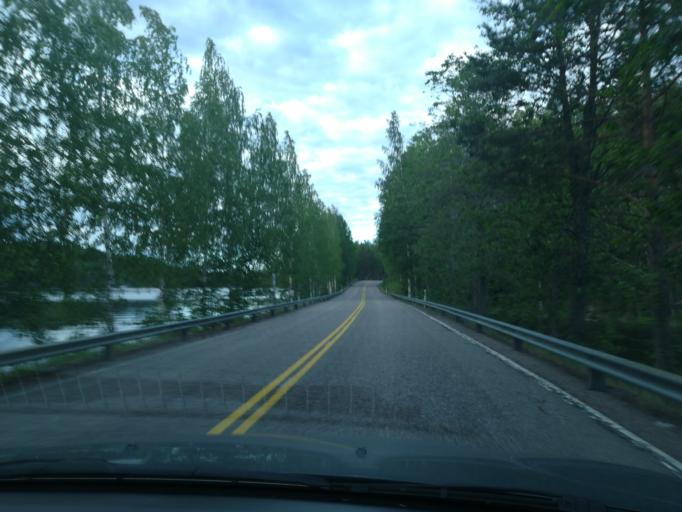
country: FI
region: Southern Savonia
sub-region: Mikkeli
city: Puumala
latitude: 61.5600
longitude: 27.9736
